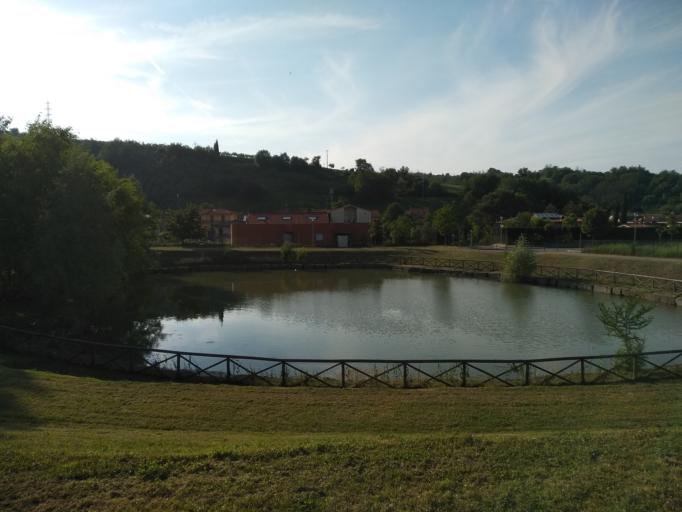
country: IT
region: Tuscany
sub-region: Province of Arezzo
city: San Giovanni Valdarno
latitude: 43.5586
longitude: 11.5277
